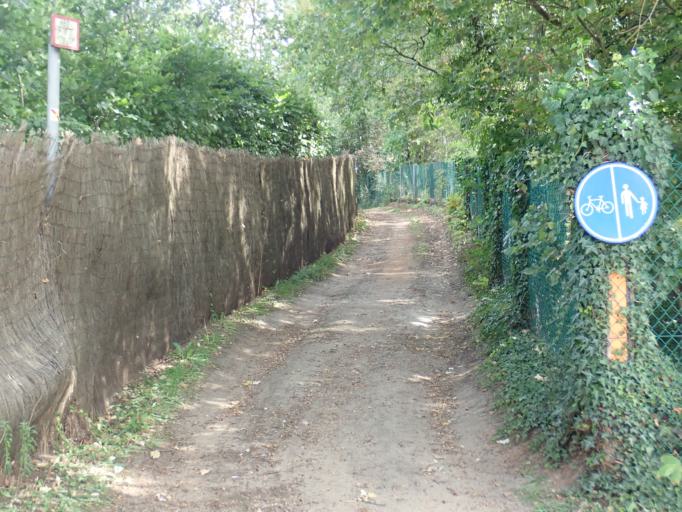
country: BE
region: Flanders
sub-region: Provincie Antwerpen
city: Lille
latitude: 51.2322
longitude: 4.8264
